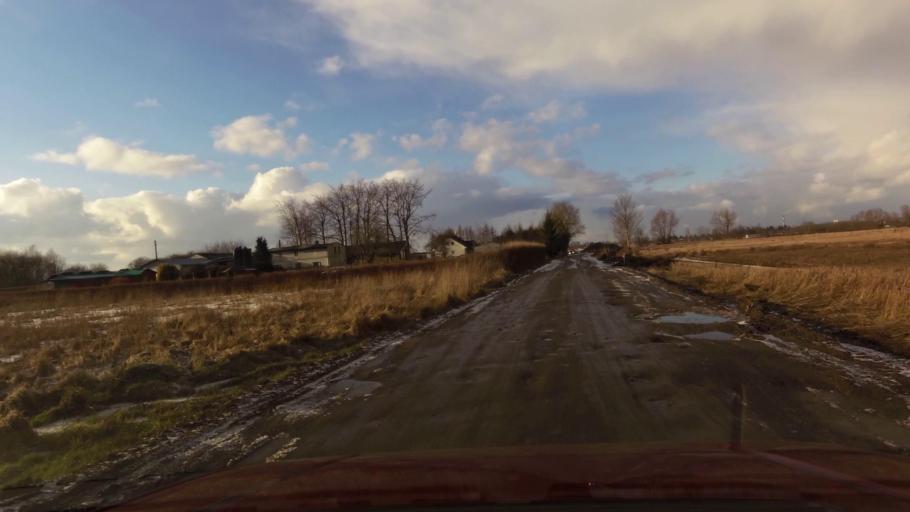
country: PL
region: West Pomeranian Voivodeship
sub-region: Koszalin
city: Koszalin
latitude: 54.1620
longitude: 16.1779
